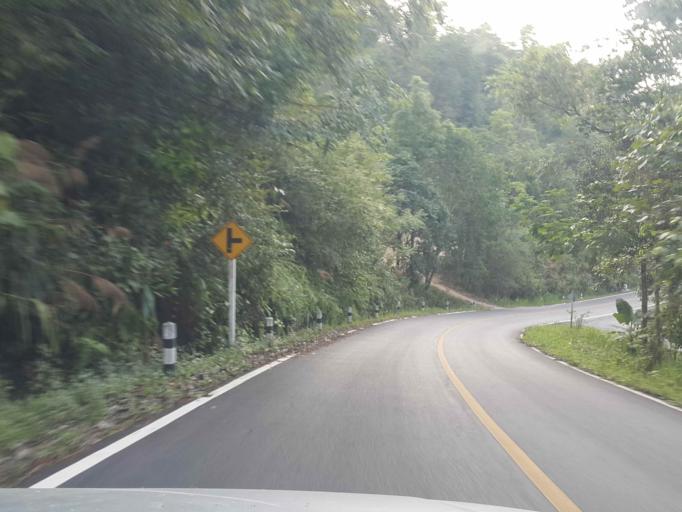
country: TH
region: Chiang Mai
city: Mae On
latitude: 18.9484
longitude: 99.3522
